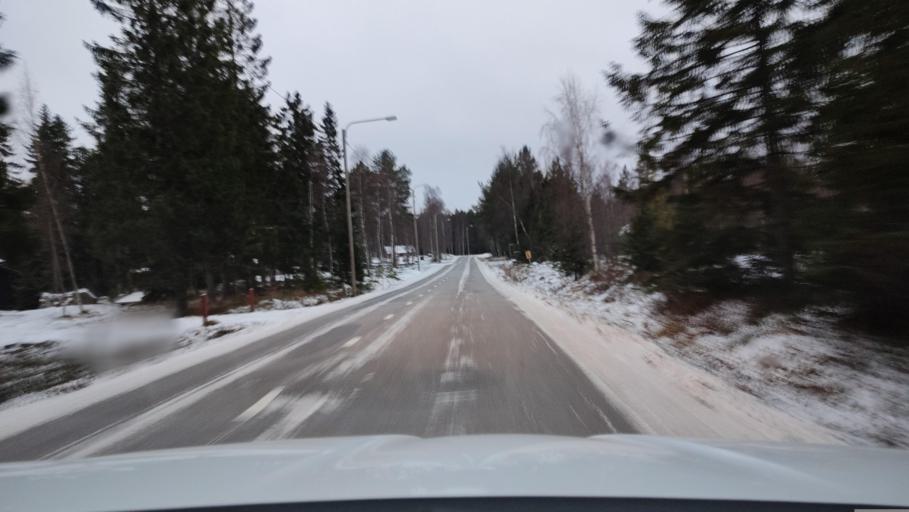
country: FI
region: Ostrobothnia
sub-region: Vaasa
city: Replot
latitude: 63.3555
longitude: 21.3033
